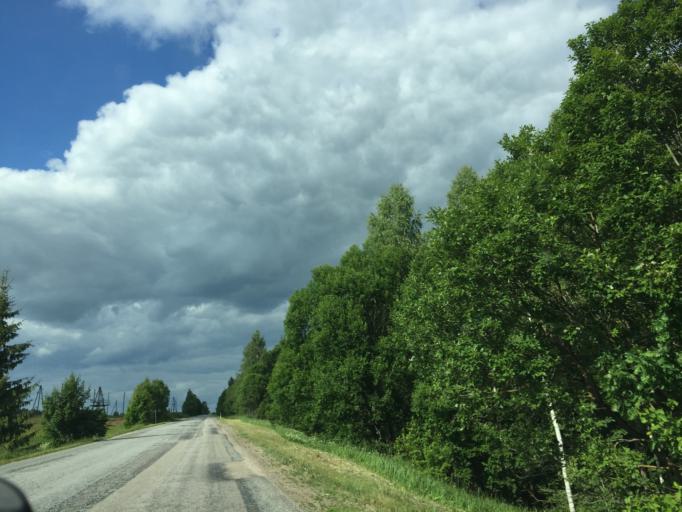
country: LV
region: Skriveri
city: Skriveri
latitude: 56.8157
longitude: 25.1171
